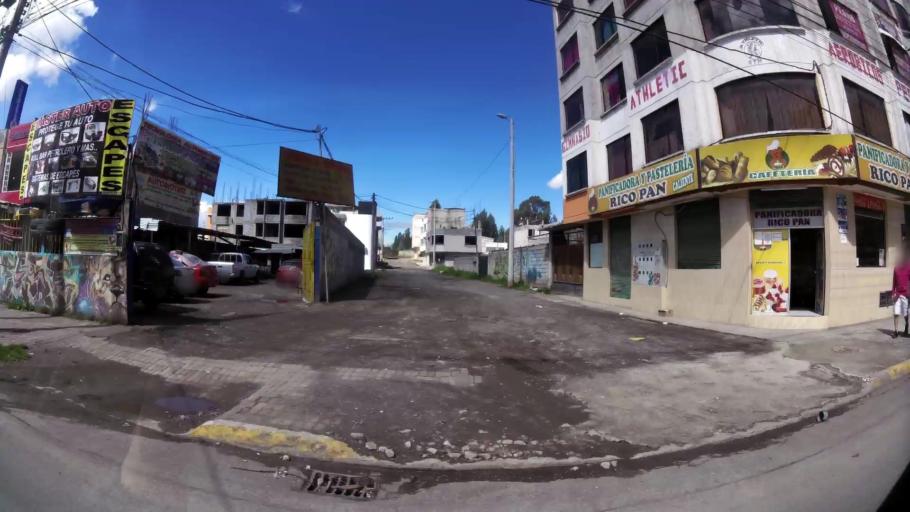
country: EC
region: Pichincha
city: Quito
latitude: -0.2981
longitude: -78.5492
